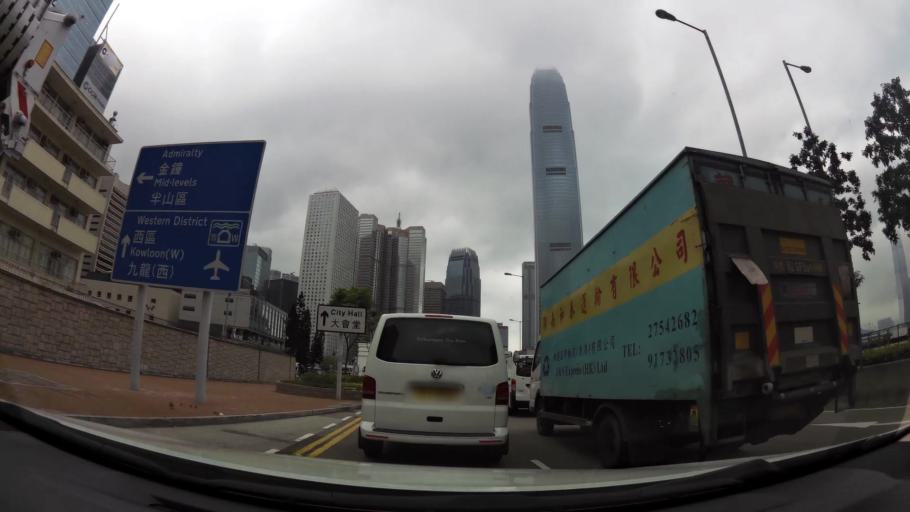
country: HK
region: Central and Western
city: Central
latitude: 22.2827
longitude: 114.1632
